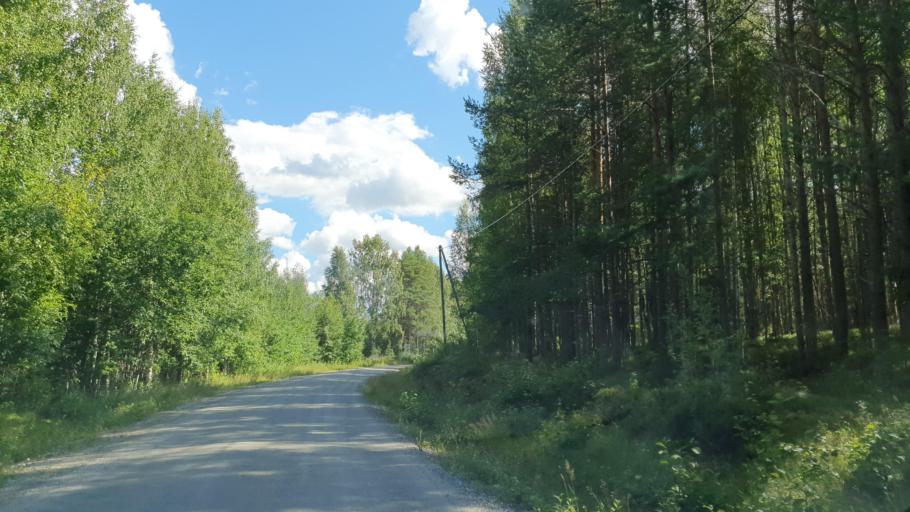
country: FI
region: Kainuu
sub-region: Kehys-Kainuu
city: Kuhmo
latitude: 64.1029
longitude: 29.4012
